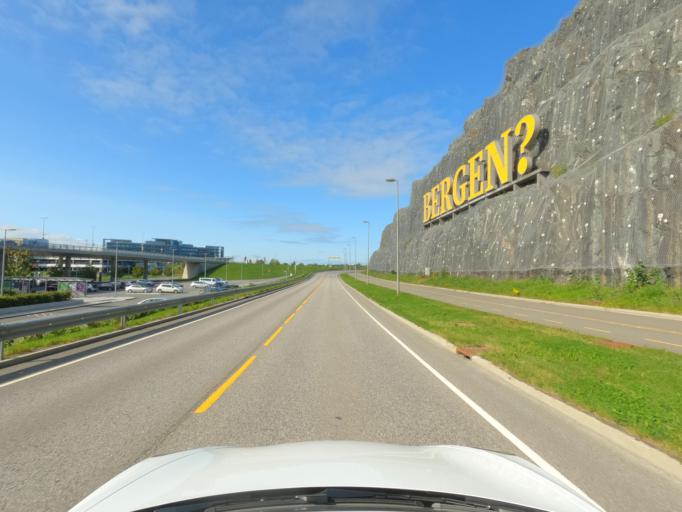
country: NO
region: Hordaland
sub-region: Bergen
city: Ytrebygda
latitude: 60.2880
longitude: 5.2340
